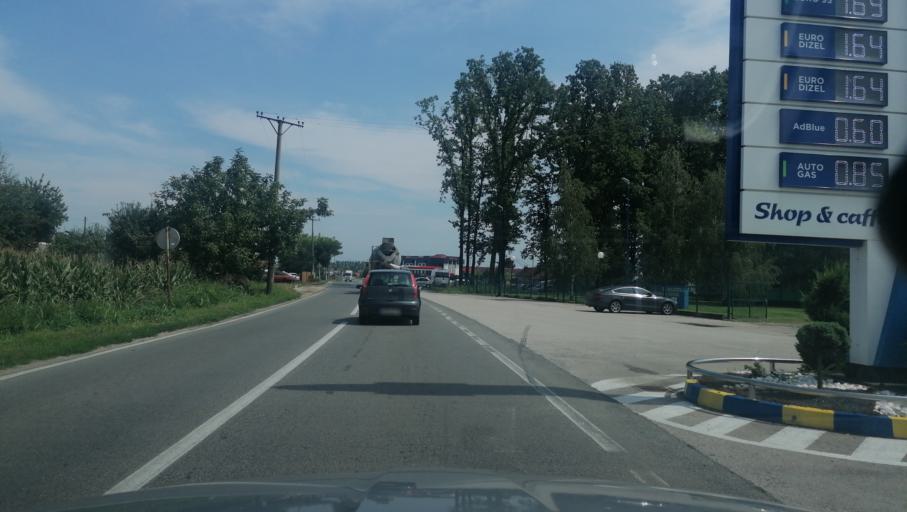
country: BA
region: Republika Srpska
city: Velika Obarska
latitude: 44.7689
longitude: 19.1592
